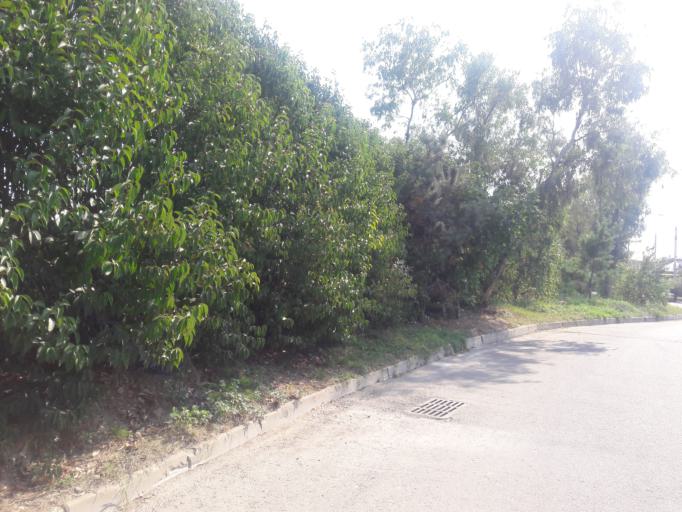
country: RU
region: Krasnodarskiy
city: Vysokoye
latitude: 43.3938
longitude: 40.0024
